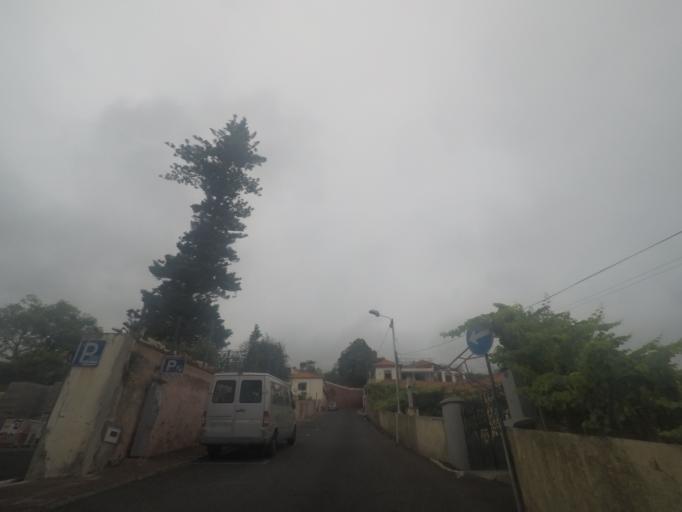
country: PT
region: Madeira
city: Camara de Lobos
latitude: 32.6720
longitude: -16.9798
